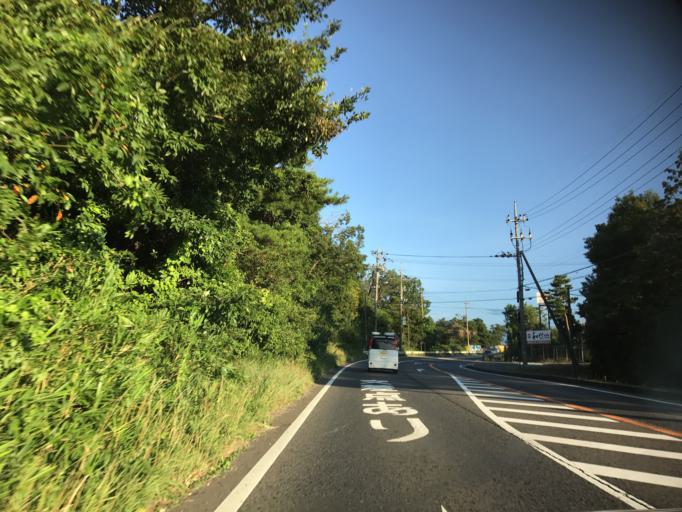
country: JP
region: Shiga Prefecture
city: Hino
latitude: 35.0372
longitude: 136.2444
